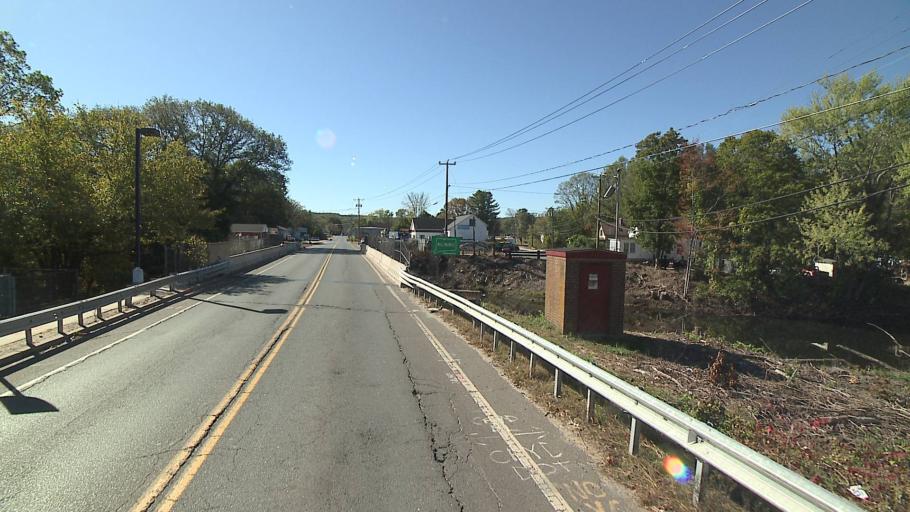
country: US
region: Connecticut
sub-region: Windham County
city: Willimantic
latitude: 41.7202
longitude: -72.1955
